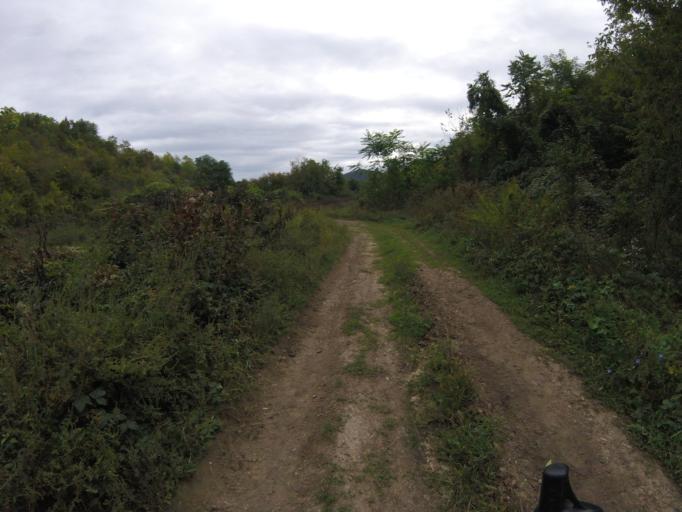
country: HU
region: Pest
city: Szob
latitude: 47.8302
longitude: 18.8132
